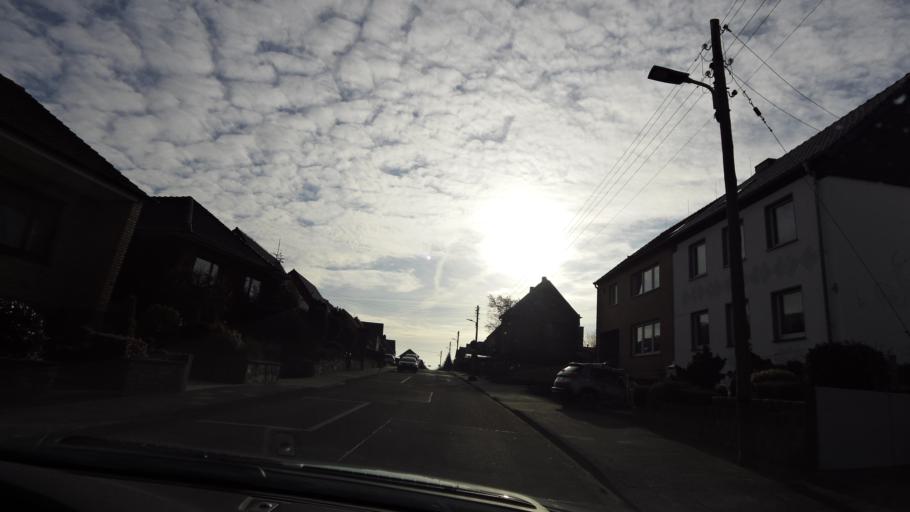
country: DE
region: North Rhine-Westphalia
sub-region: Regierungsbezirk Koln
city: Ubach-Palenberg
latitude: 50.9230
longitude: 6.0607
